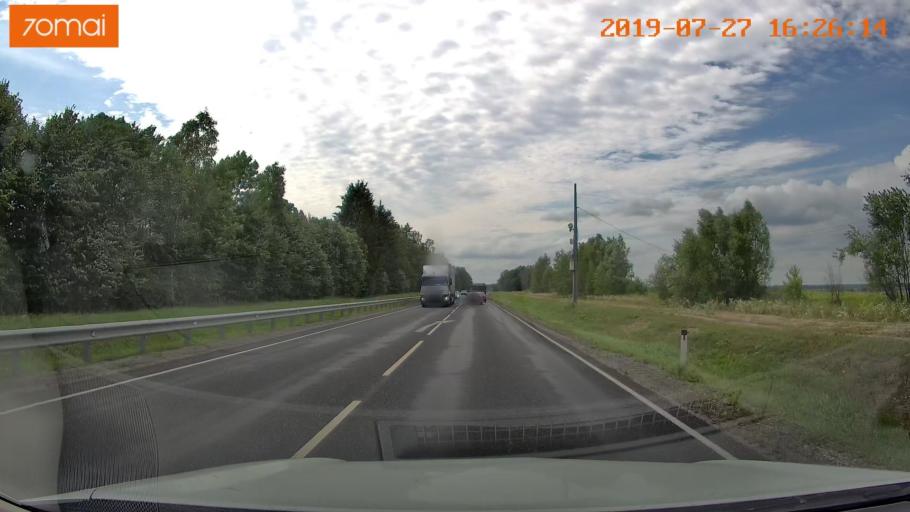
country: RU
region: Kaliningrad
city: Zheleznodorozhnyy
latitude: 54.6397
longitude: 21.4148
